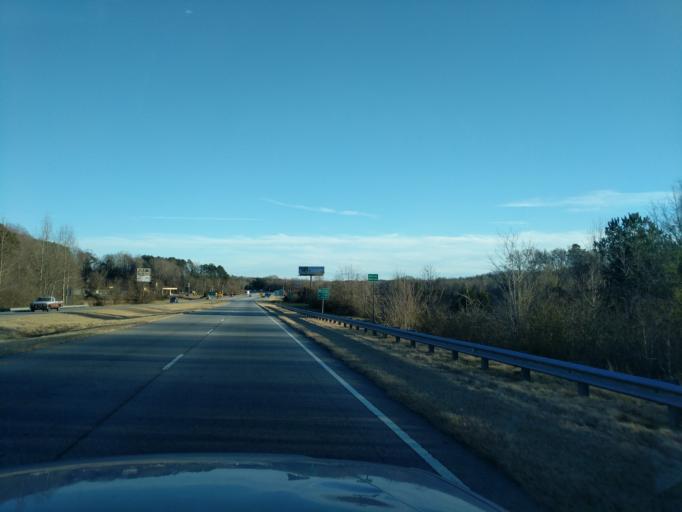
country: US
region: Georgia
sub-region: Stephens County
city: Toccoa
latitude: 34.5456
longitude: -83.3655
